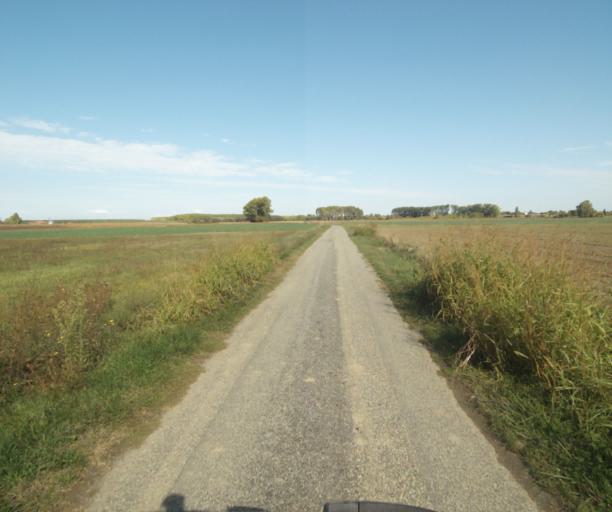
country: FR
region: Midi-Pyrenees
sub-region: Departement du Tarn-et-Garonne
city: Finhan
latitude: 43.8912
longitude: 1.2210
